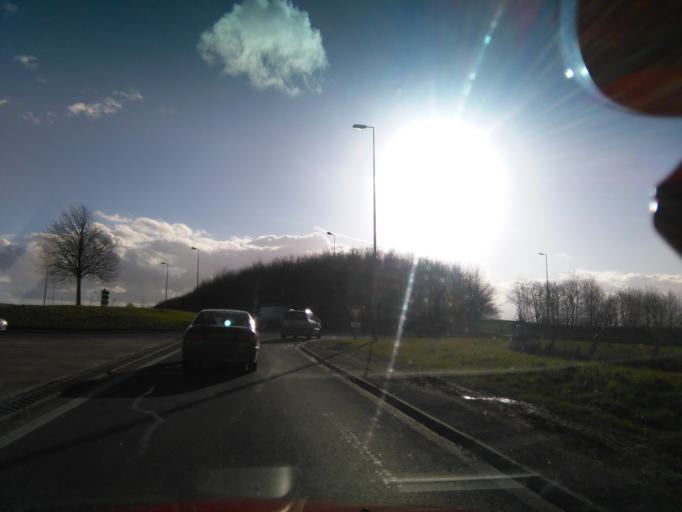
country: FR
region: Lower Normandy
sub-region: Departement du Calvados
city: Bretteville-sur-Odon
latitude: 49.1537
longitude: -0.4160
